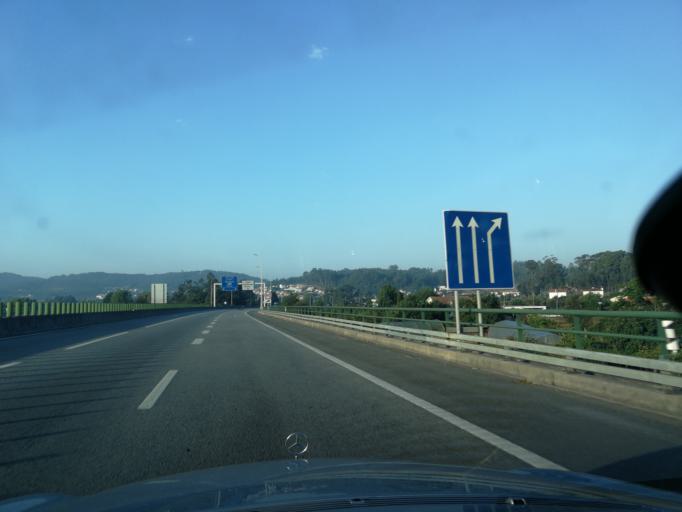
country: PT
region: Braga
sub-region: Braga
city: Braga
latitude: 41.5197
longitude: -8.4233
